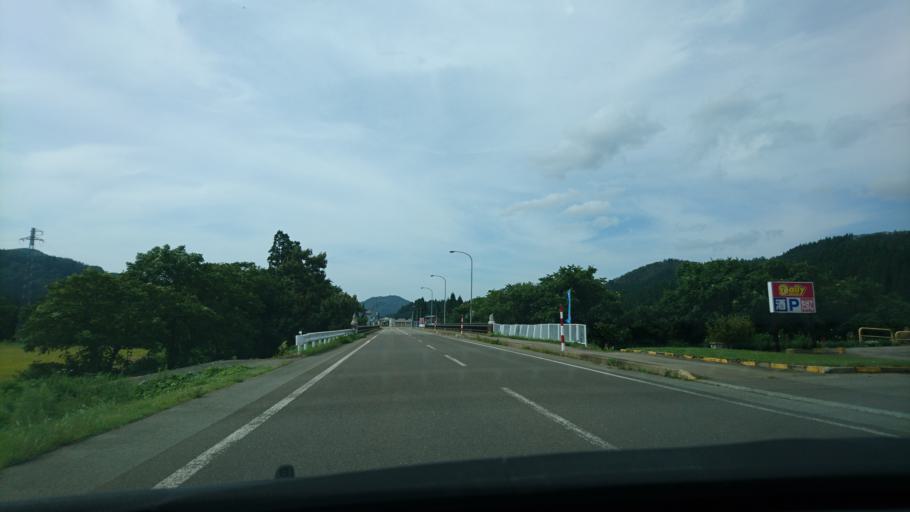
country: JP
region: Akita
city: Yuzawa
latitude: 39.1846
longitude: 140.6362
